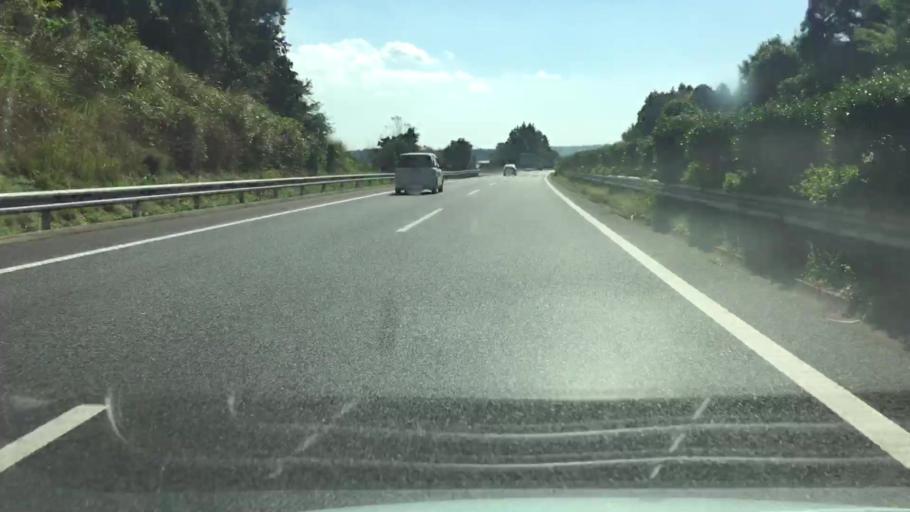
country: JP
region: Ibaraki
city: Tomobe
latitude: 36.3361
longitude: 140.2838
